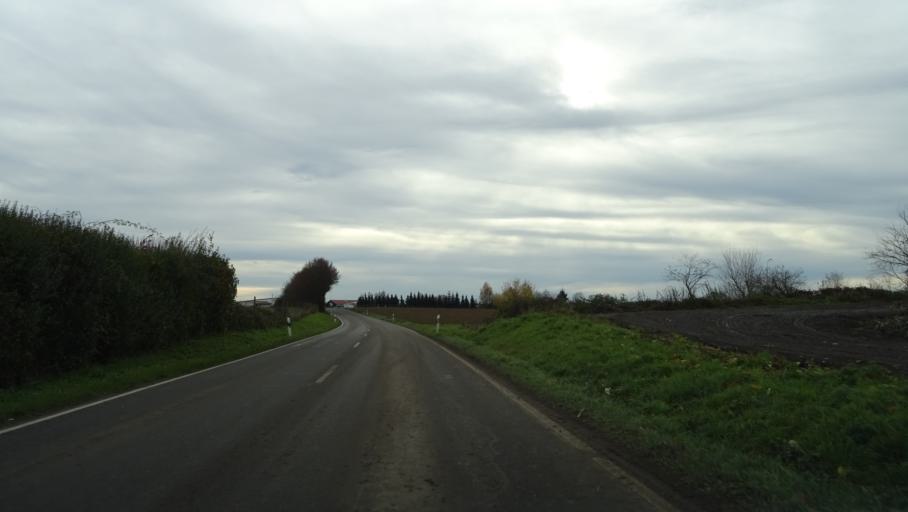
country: DE
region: Baden-Wuerttemberg
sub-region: Karlsruhe Region
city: Fahrenbach
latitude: 49.4023
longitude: 9.1209
